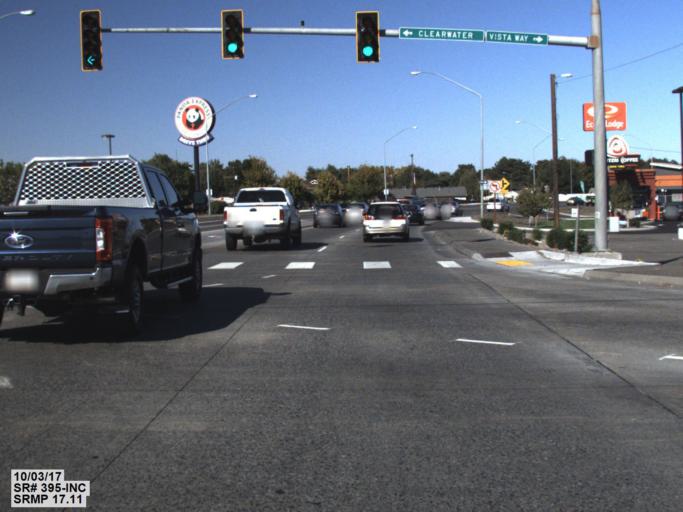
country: US
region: Washington
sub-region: Benton County
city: Kennewick
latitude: 46.2122
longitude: -119.1588
